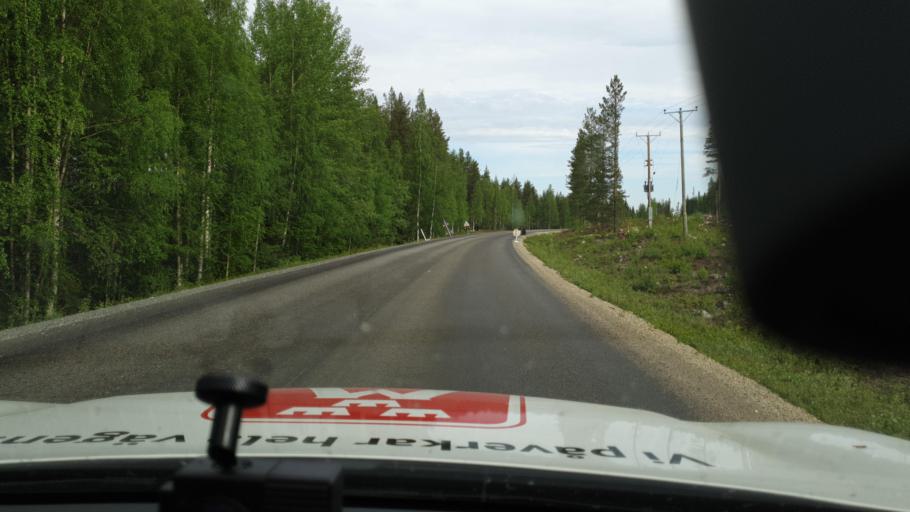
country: SE
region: Vaesterbotten
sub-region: Lycksele Kommun
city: Lycksele
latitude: 64.8616
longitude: 18.7228
